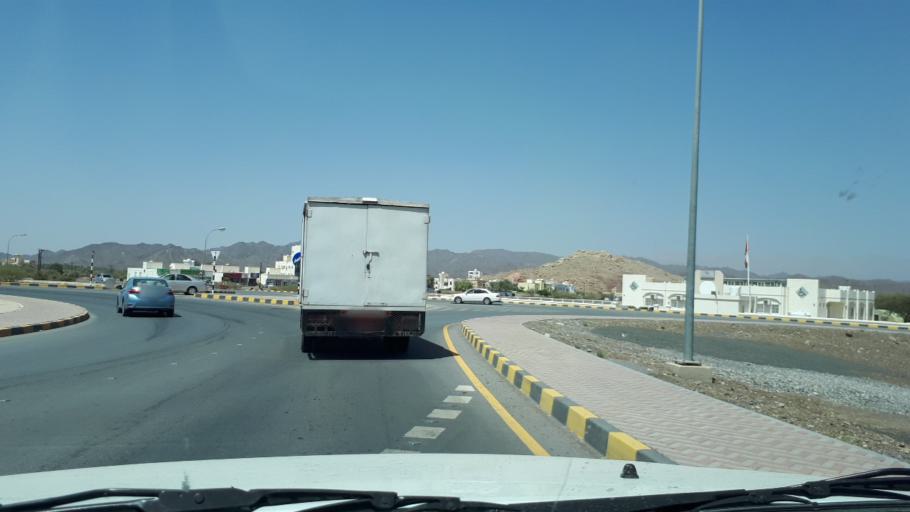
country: OM
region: Muhafazat ad Dakhiliyah
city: Bahla'
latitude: 22.9989
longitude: 57.3169
